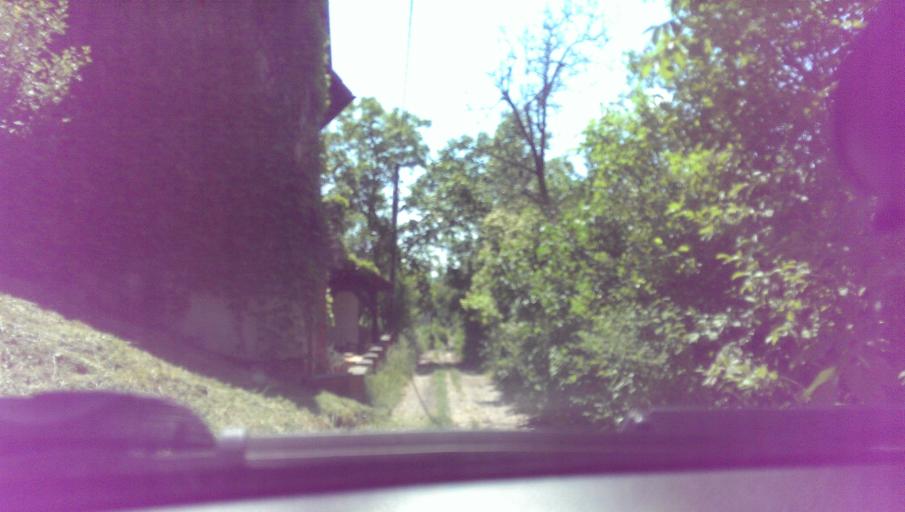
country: CZ
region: Zlin
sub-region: Okres Uherske Hradiste
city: Uherske Hradiste
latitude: 49.0689
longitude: 17.4903
